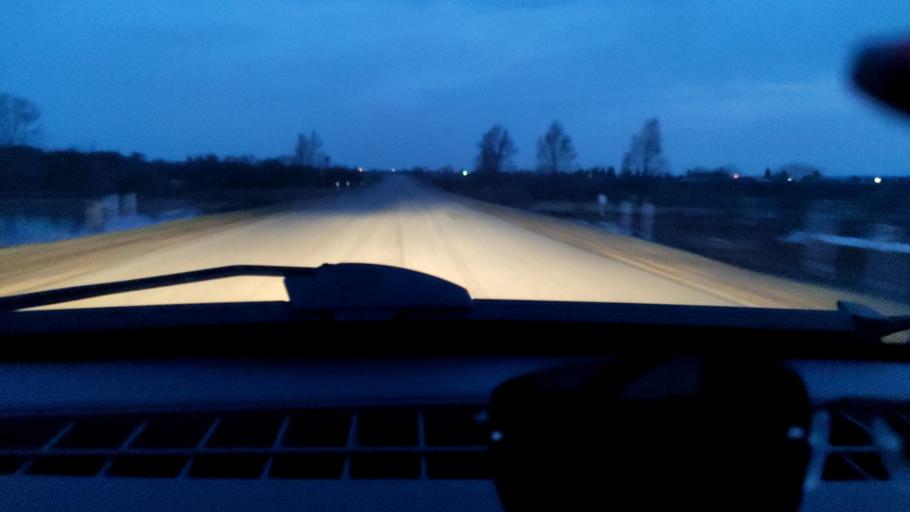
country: RU
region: Bashkortostan
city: Kabakovo
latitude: 54.4887
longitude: 56.1880
